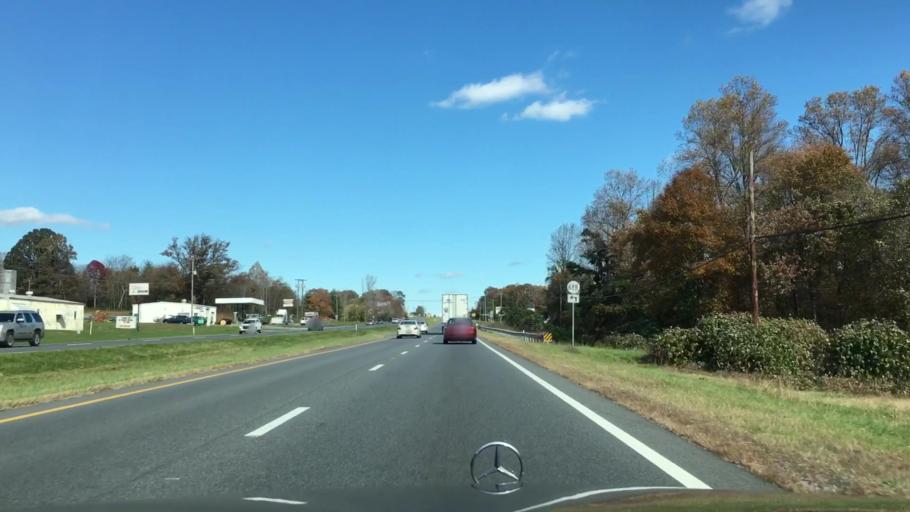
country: US
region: Virginia
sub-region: Campbell County
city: Rustburg
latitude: 37.2718
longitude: -79.1739
